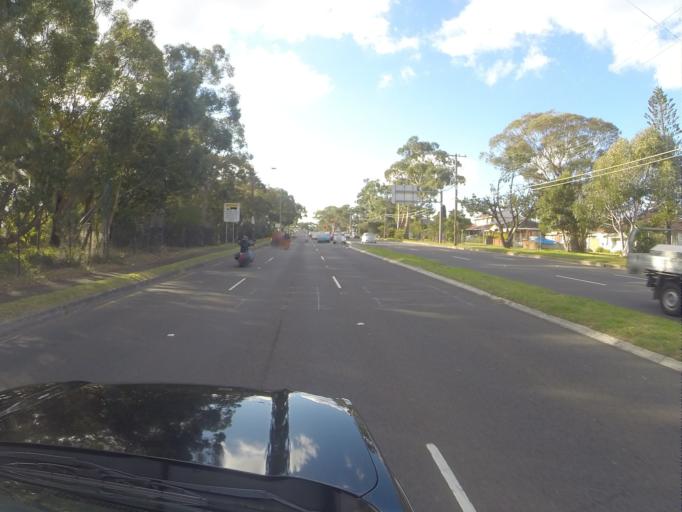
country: AU
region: New South Wales
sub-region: Sutherland Shire
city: Kareela
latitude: -34.0213
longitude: 151.0900
